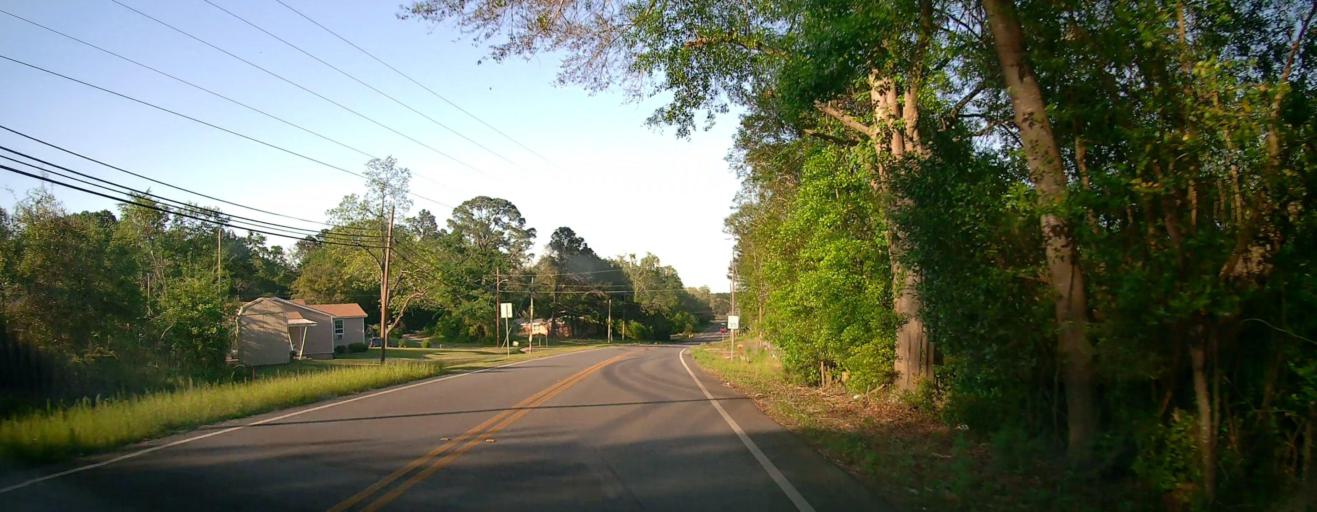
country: US
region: Georgia
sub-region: Macon County
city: Oglethorpe
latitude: 32.2896
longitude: -84.0668
